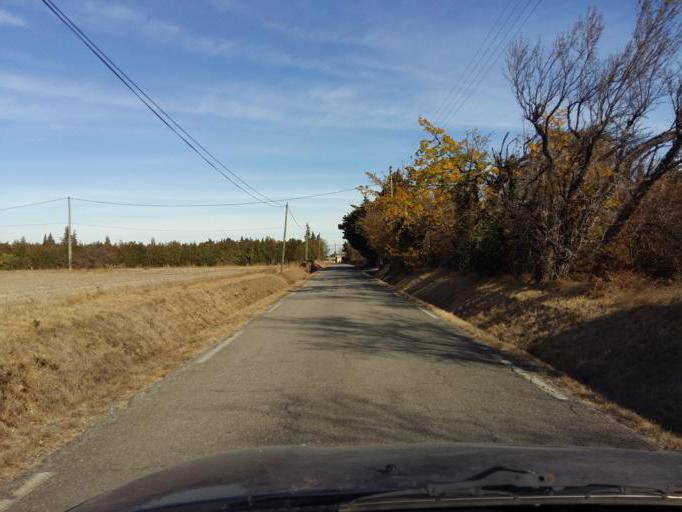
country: FR
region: Provence-Alpes-Cote d'Azur
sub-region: Departement du Vaucluse
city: Serignan-du-Comtat
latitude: 44.1572
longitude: 4.8359
